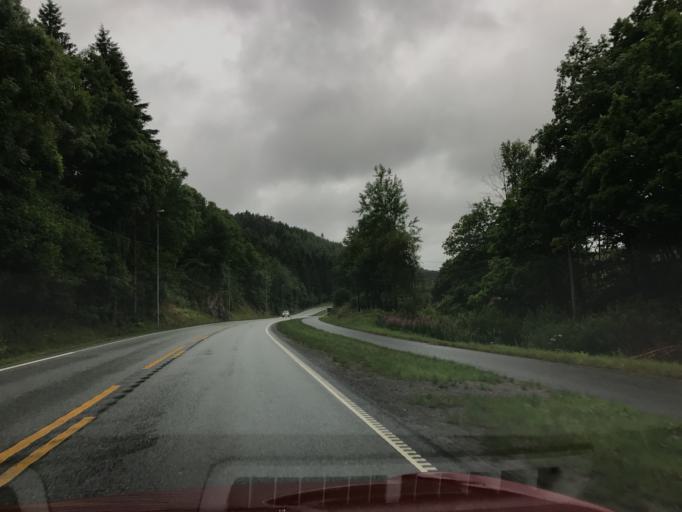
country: NO
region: Vest-Agder
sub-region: Mandal
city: Mandal
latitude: 58.0398
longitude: 7.5428
